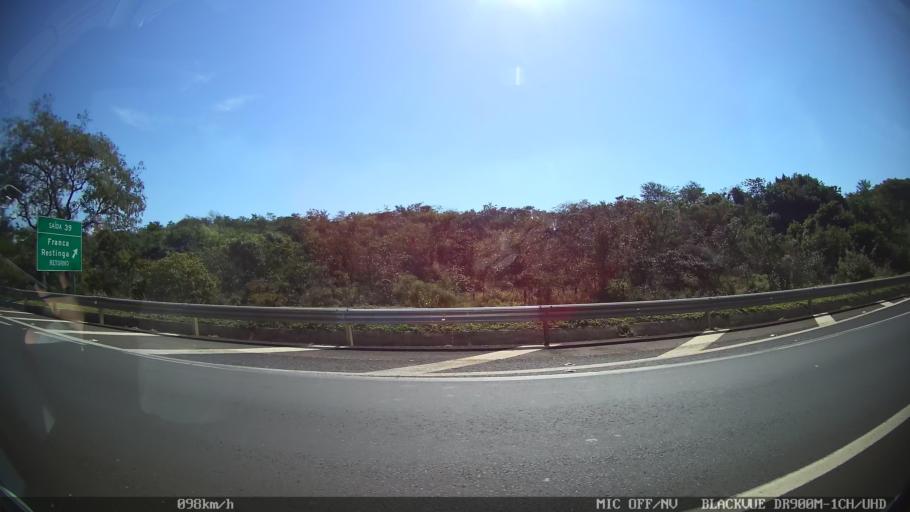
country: BR
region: Sao Paulo
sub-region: Franca
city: Franca
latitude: -20.5566
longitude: -47.4367
